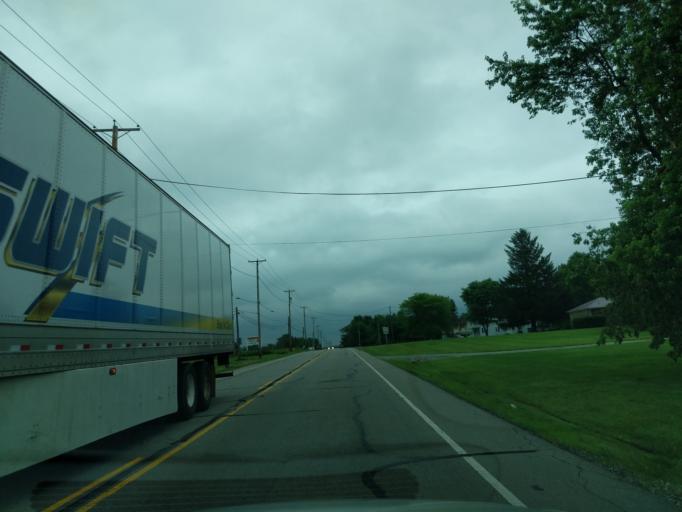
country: US
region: Indiana
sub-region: Madison County
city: Alexandria
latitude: 40.2779
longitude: -85.6596
